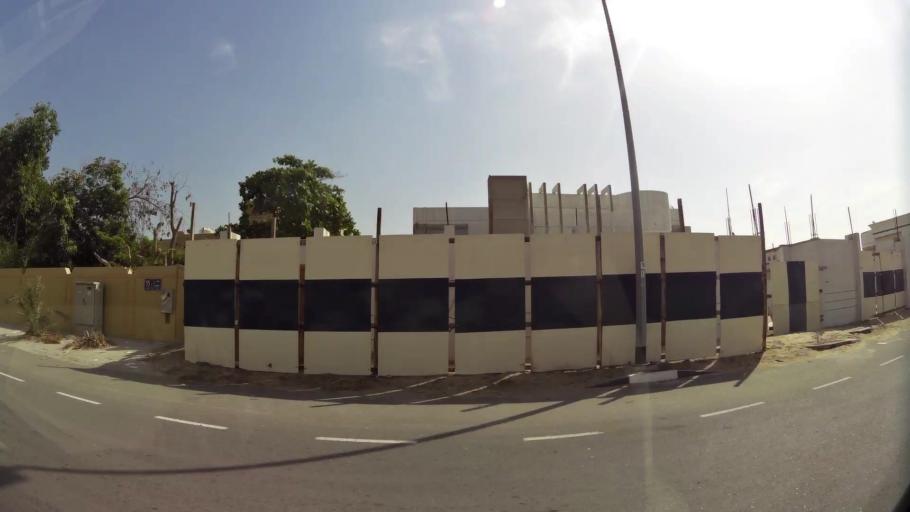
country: AE
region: Ash Shariqah
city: Sharjah
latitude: 25.2774
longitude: 55.4011
